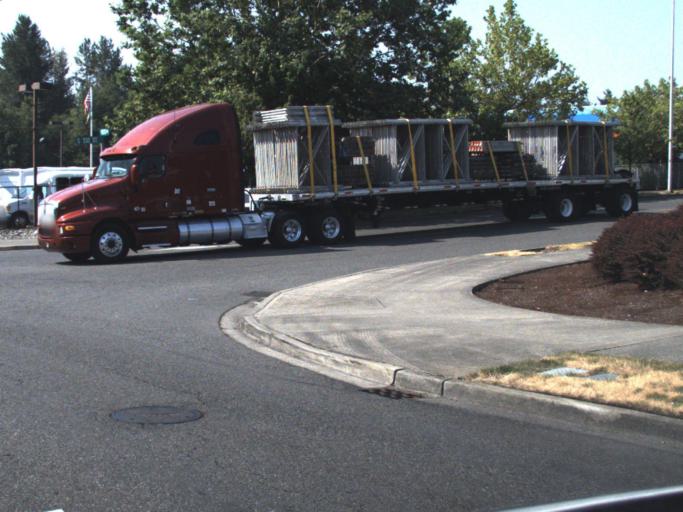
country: US
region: Washington
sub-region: King County
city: Federal Way
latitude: 47.3044
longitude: -122.3135
